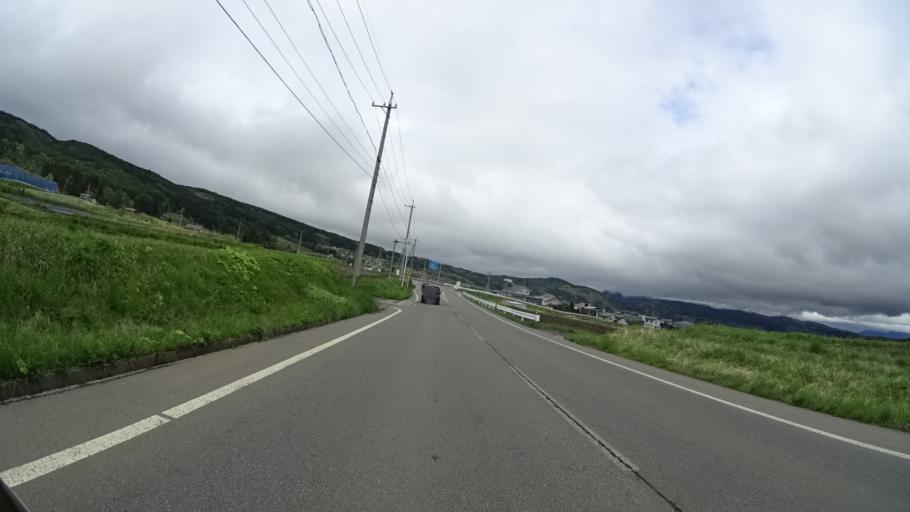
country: JP
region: Nagano
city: Nagano-shi
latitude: 36.7310
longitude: 138.2086
